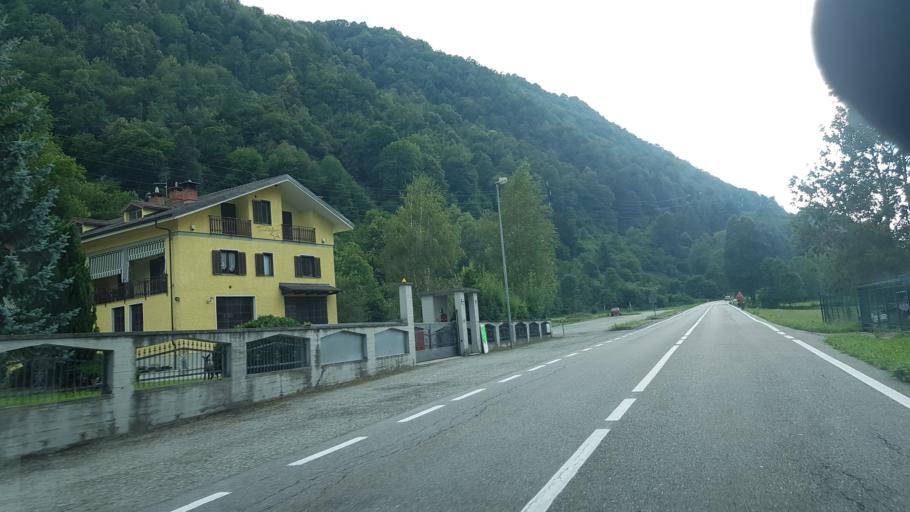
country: IT
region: Piedmont
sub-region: Provincia di Cuneo
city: Frassino
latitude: 44.5690
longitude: 7.2919
